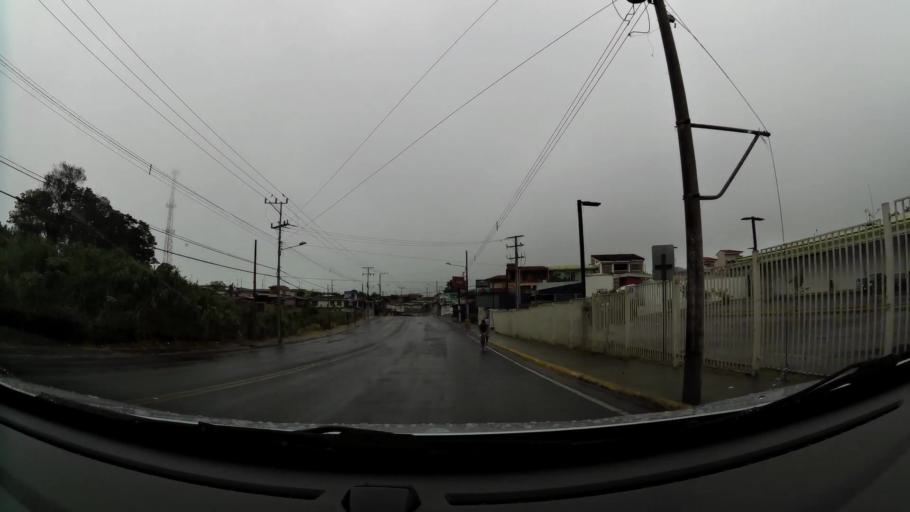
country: CR
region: Cartago
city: Paraiso
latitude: 9.8397
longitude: -83.8721
